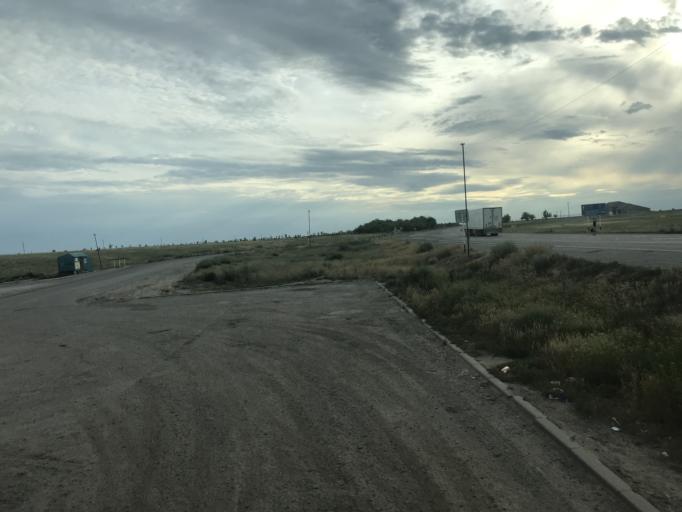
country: KZ
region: Aqtoebe
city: Martuk
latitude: 50.2075
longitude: 56.4693
